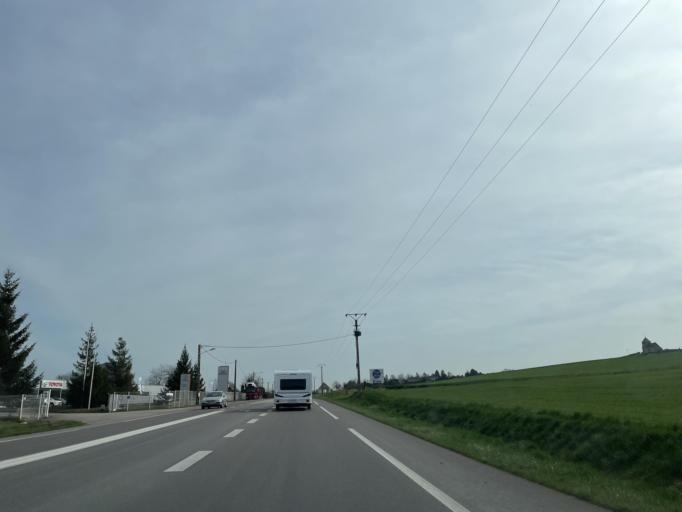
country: FR
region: Champagne-Ardenne
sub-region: Departement de l'Aube
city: Romilly-sur-Seine
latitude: 48.5151
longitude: 3.6459
